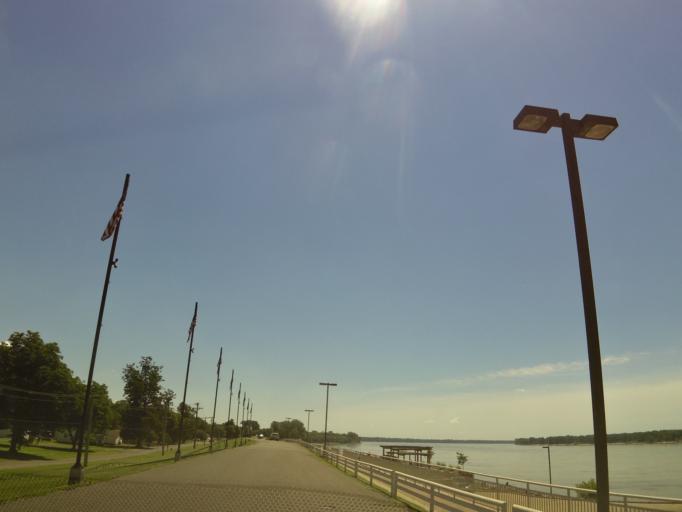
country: US
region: Missouri
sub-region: New Madrid County
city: New Madrid
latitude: 36.5834
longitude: -89.5337
